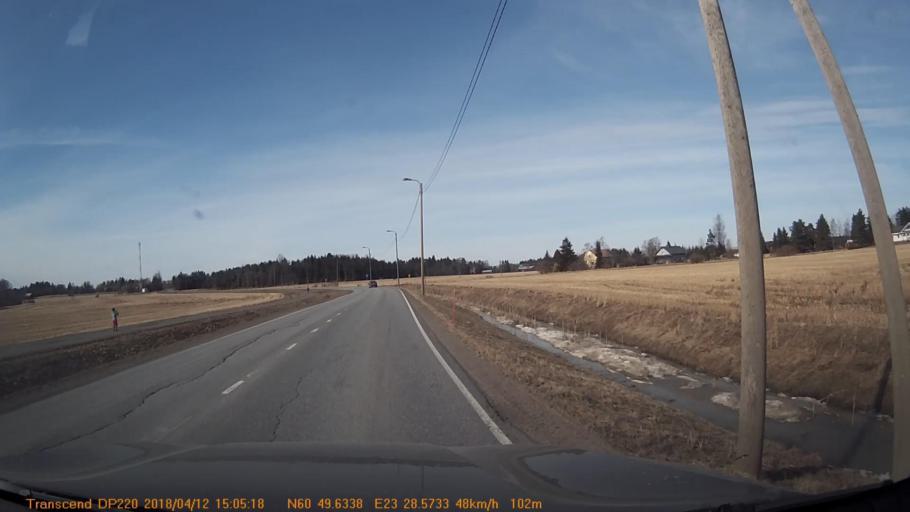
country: FI
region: Haeme
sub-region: Forssa
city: Jokioinen
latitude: 60.8274
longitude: 23.4761
